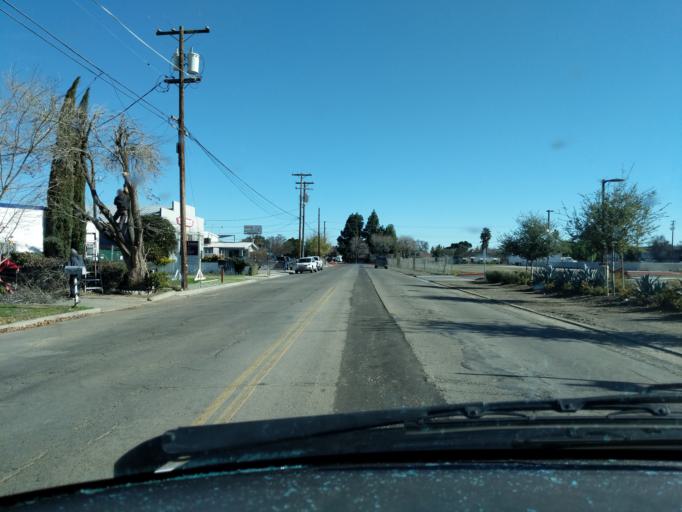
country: US
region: California
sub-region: Merced County
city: Los Banos
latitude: 37.0601
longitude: -120.8374
